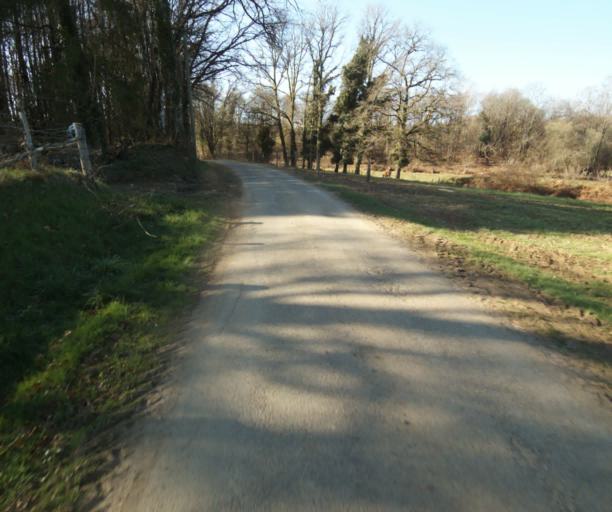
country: FR
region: Limousin
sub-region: Departement de la Correze
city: Saint-Clement
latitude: 45.3785
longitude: 1.6542
